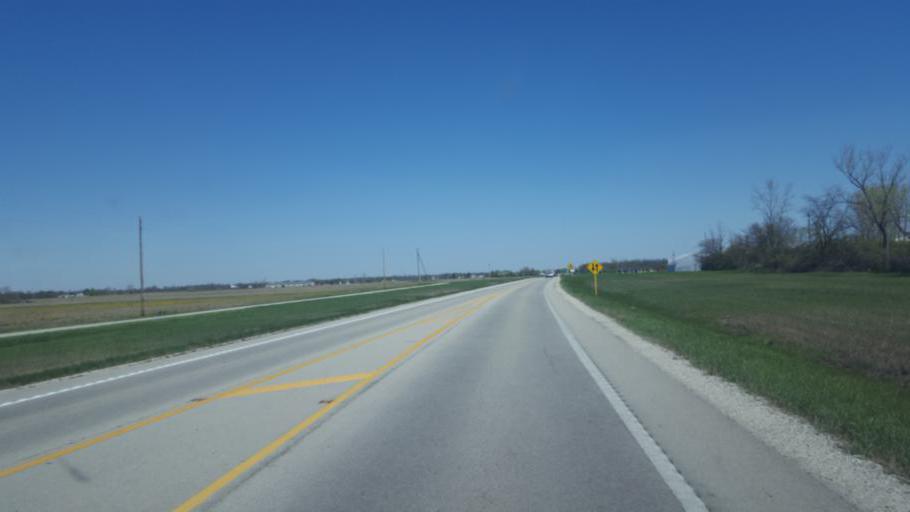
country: US
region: Ohio
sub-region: Sandusky County
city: Stony Prairie
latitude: 41.3314
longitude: -83.1680
